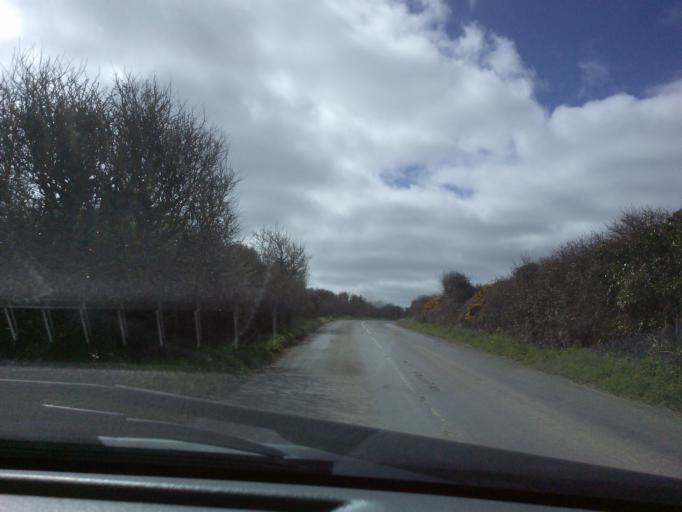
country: GB
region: England
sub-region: Cornwall
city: St. Buryan
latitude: 50.0638
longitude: -5.5933
